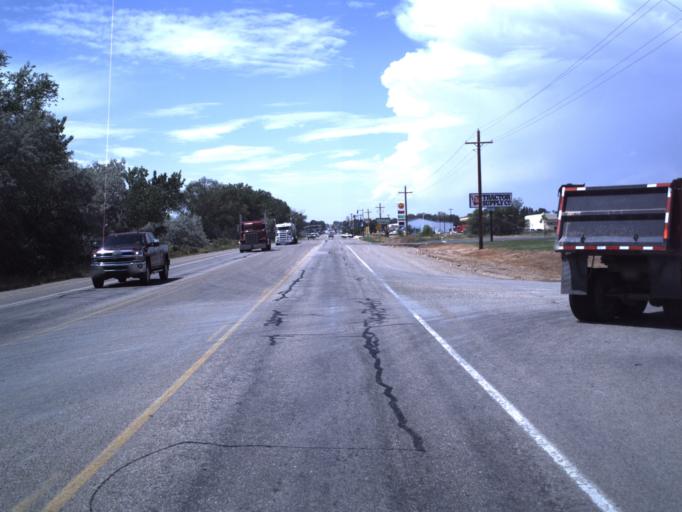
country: US
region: Utah
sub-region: Duchesne County
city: Roosevelt
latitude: 40.3023
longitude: -109.9658
